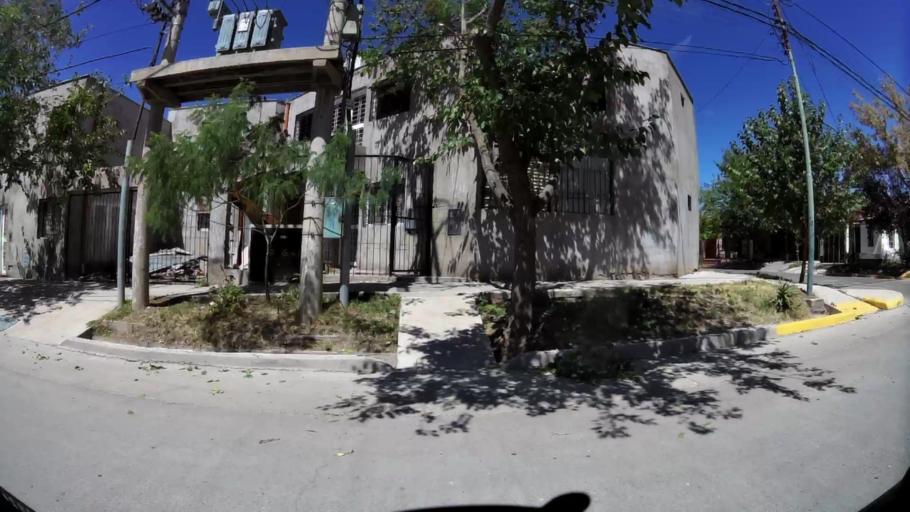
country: AR
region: Mendoza
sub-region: Departamento de Godoy Cruz
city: Godoy Cruz
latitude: -32.9490
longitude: -68.8644
